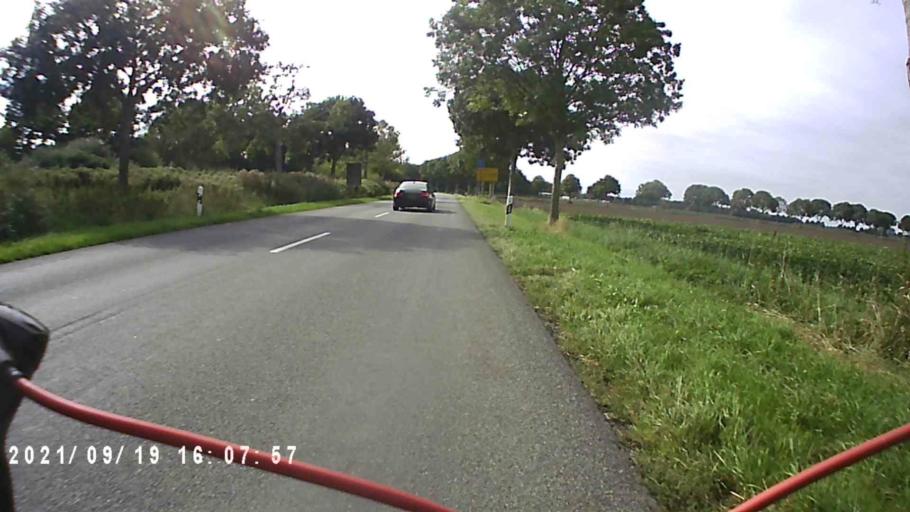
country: DE
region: Lower Saxony
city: Bunde
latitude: 53.1819
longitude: 7.2319
